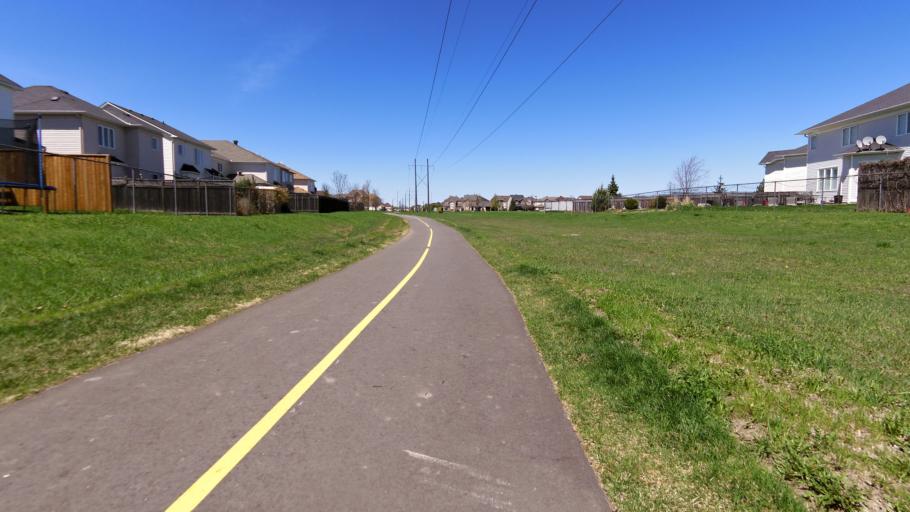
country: CA
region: Ontario
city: Clarence-Rockland
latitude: 45.4557
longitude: -75.4709
